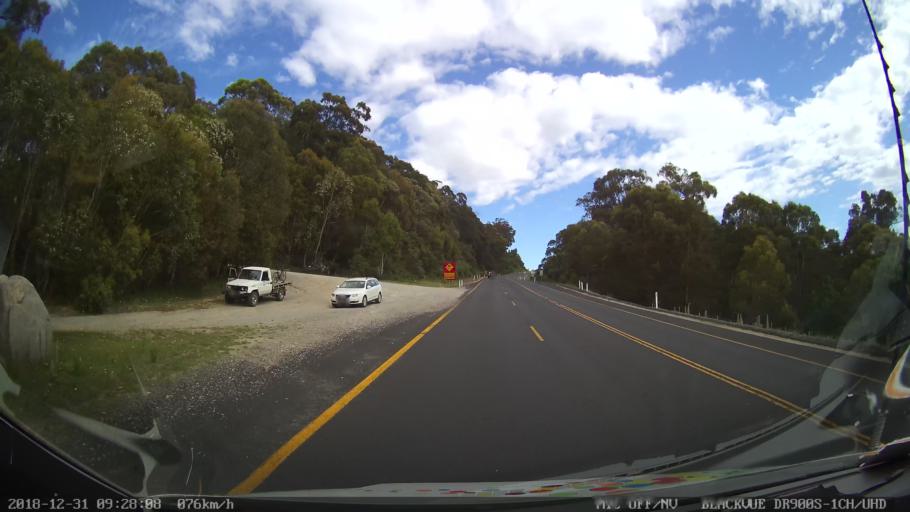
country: AU
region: New South Wales
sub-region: Snowy River
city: Jindabyne
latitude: -36.4587
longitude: 148.4761
